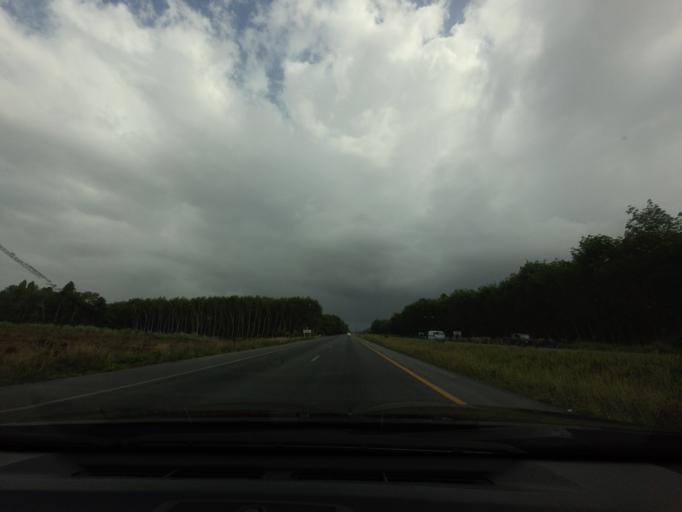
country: TH
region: Pattani
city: Mae Lan
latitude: 6.7122
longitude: 101.2280
